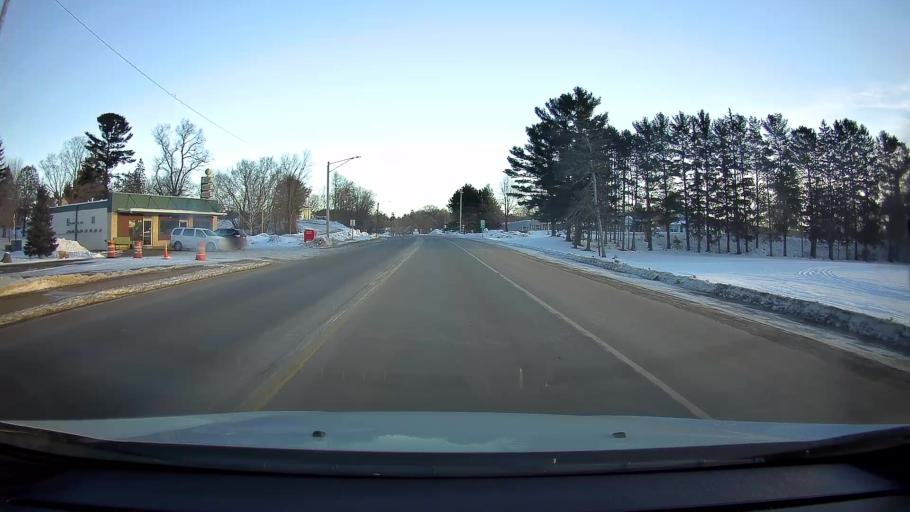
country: US
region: Wisconsin
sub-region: Barron County
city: Cumberland
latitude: 45.5411
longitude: -92.0204
